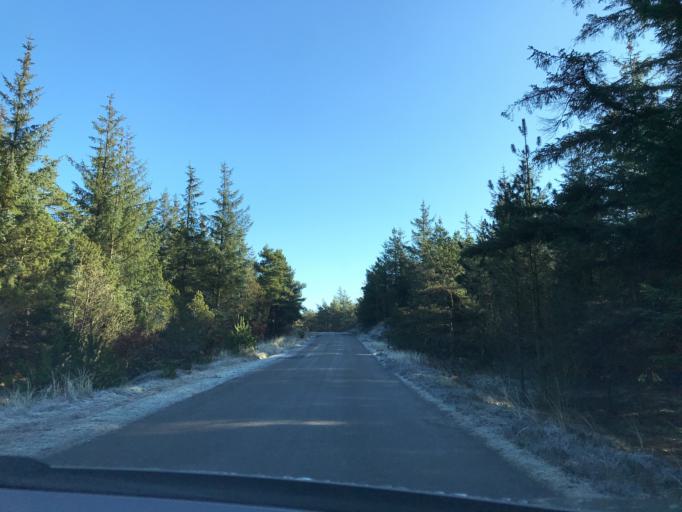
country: DK
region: South Denmark
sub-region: Varde Kommune
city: Oksbol
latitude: 55.7926
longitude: 8.1992
